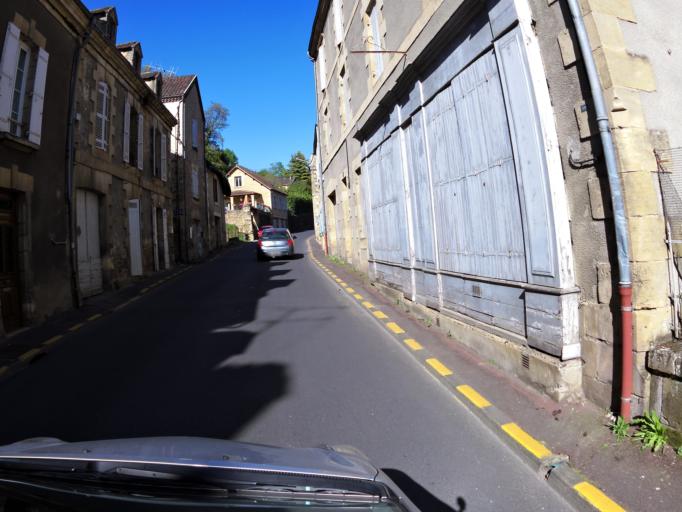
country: FR
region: Aquitaine
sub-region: Departement de la Dordogne
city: Sarlat-la-Caneda
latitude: 44.8914
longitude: 1.2192
